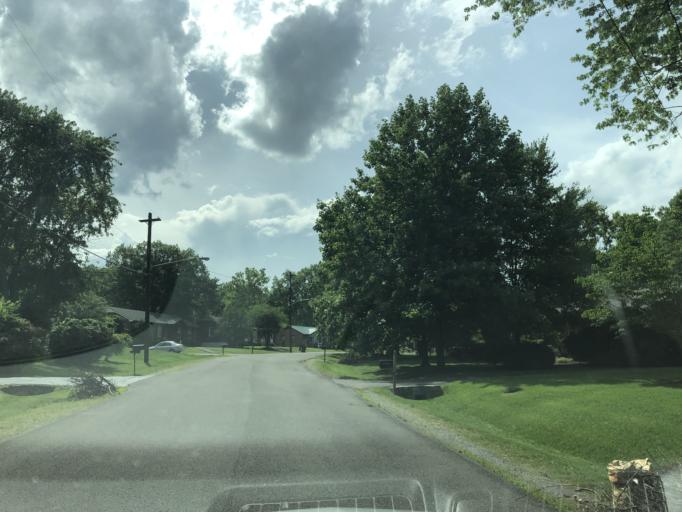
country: US
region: Tennessee
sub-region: Davidson County
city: Oak Hill
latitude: 36.0838
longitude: -86.7506
